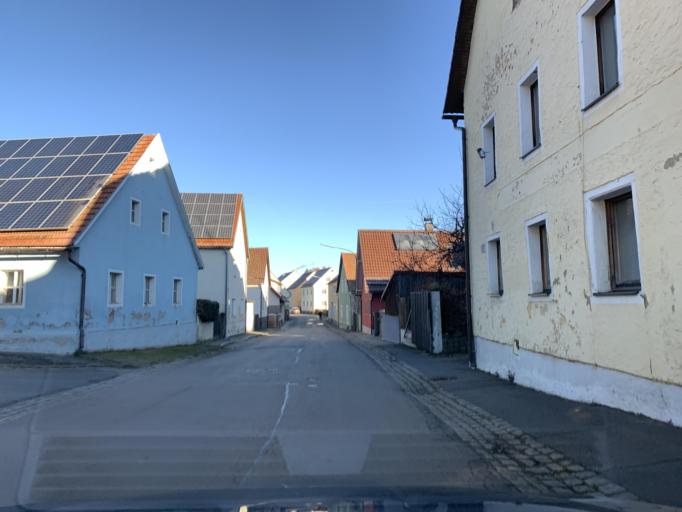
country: DE
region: Bavaria
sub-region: Upper Palatinate
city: Winklarn
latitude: 49.4275
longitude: 12.4816
